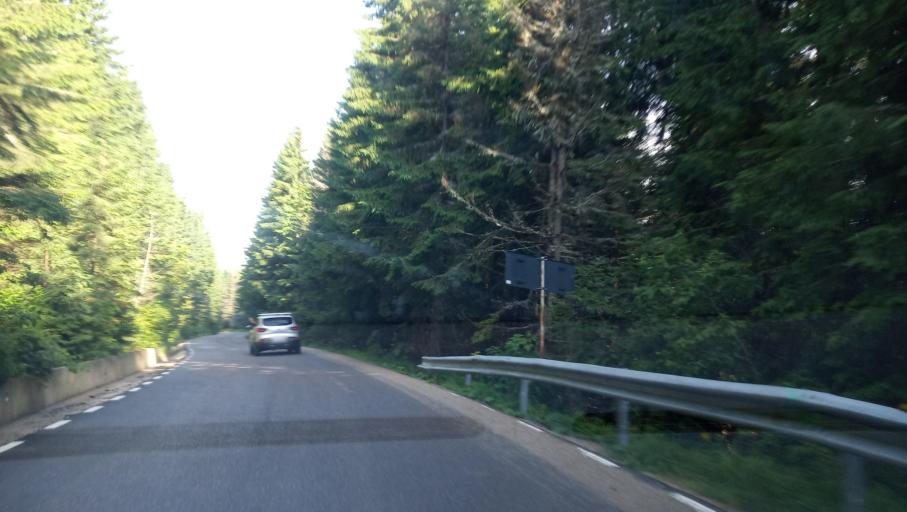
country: RO
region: Dambovita
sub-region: Comuna Moroeni
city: Glod
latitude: 45.3265
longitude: 25.4475
